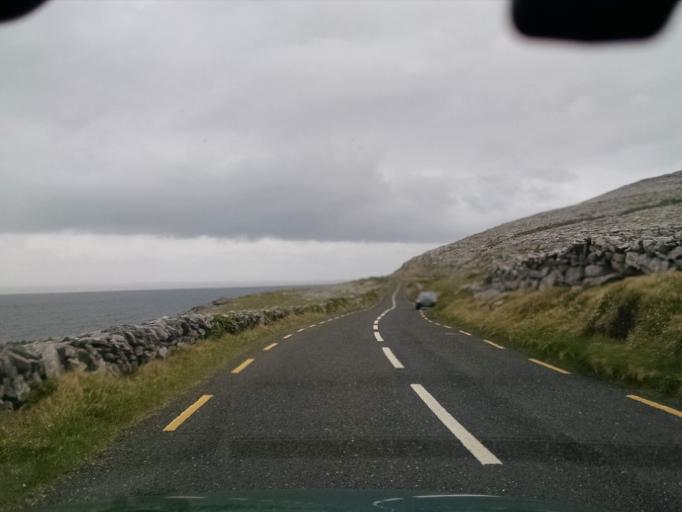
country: IE
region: Connaught
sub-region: County Galway
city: Bearna
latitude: 53.1473
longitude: -9.2714
